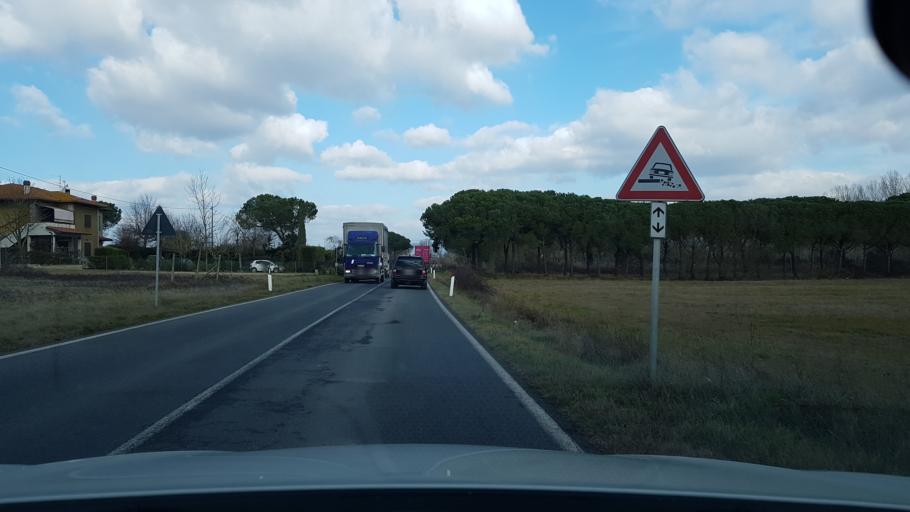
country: IT
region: Tuscany
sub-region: Province of Arezzo
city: Terontola
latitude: 43.1664
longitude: 12.0148
